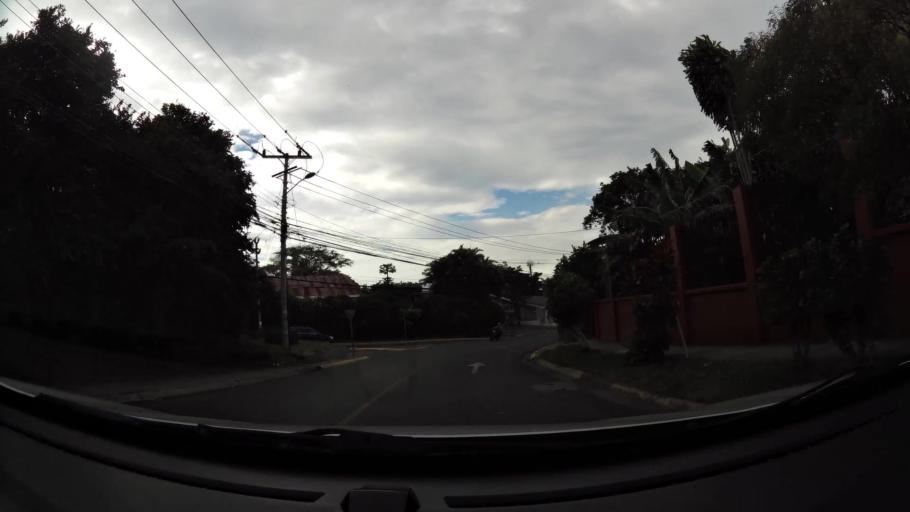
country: CR
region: San Jose
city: San Rafael
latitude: 9.9292
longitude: -84.1499
